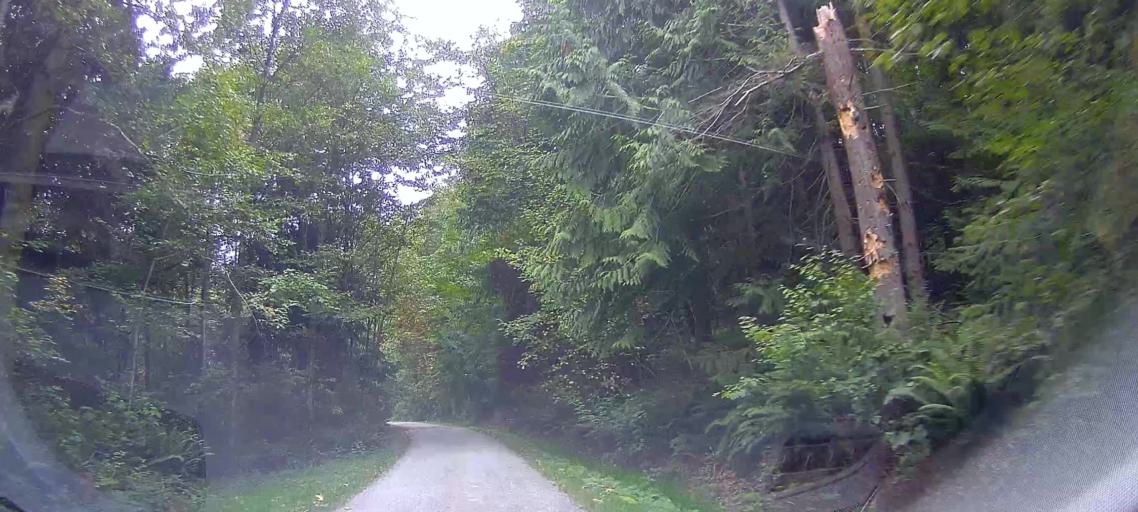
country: US
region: Washington
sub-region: Whatcom County
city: Geneva
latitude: 48.6120
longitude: -122.4345
